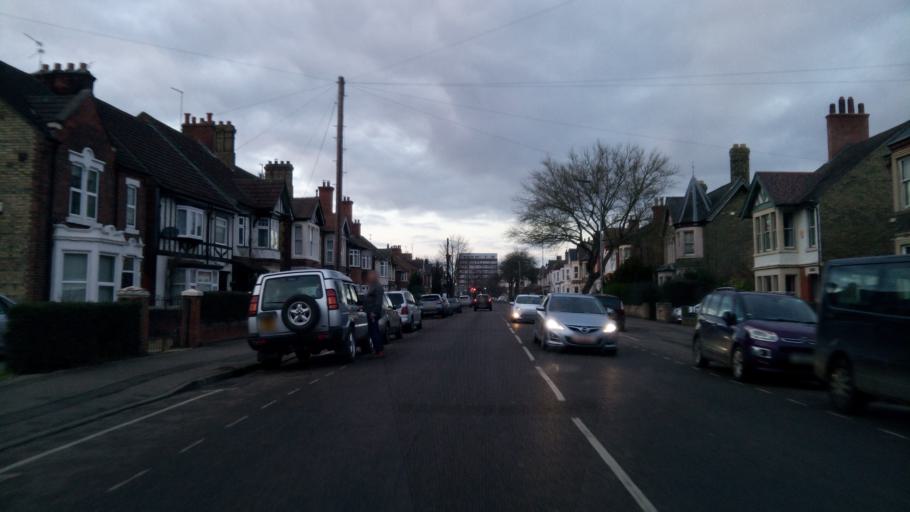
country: GB
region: England
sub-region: Peterborough
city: Peterborough
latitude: 52.5619
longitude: -0.2419
